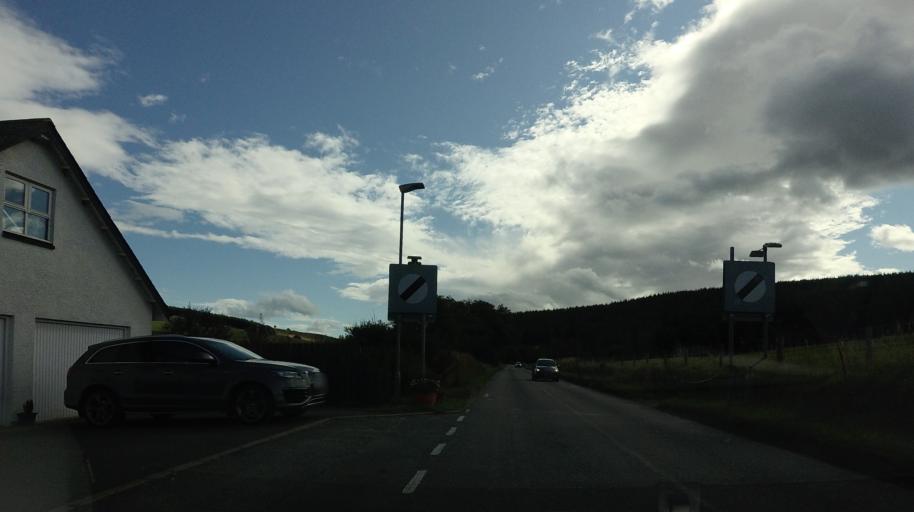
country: GB
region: Scotland
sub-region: Aberdeenshire
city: Torphins
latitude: 57.1267
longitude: -2.6779
